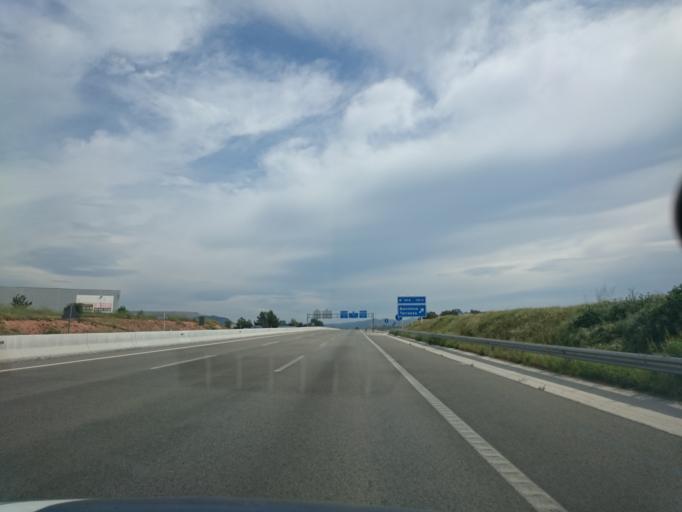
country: ES
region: Catalonia
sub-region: Provincia de Barcelona
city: Sant Fruitos de Bages
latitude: 41.7736
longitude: 1.8756
